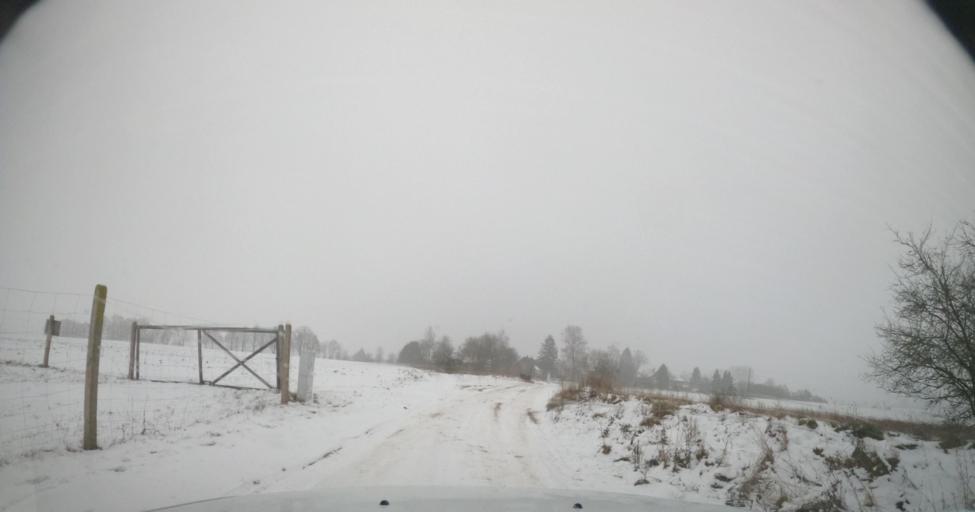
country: PL
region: West Pomeranian Voivodeship
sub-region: Powiat kamienski
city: Golczewo
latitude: 53.8692
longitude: 15.0666
